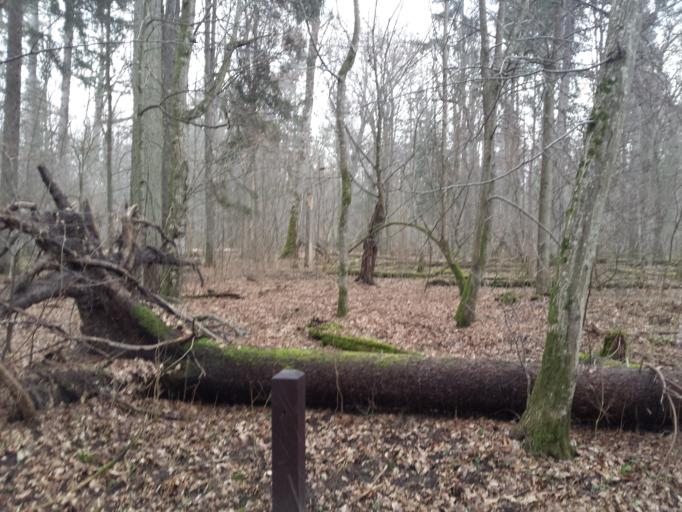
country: PL
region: Podlasie
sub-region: Powiat hajnowski
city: Bialowieza
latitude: 52.7179
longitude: 23.8436
